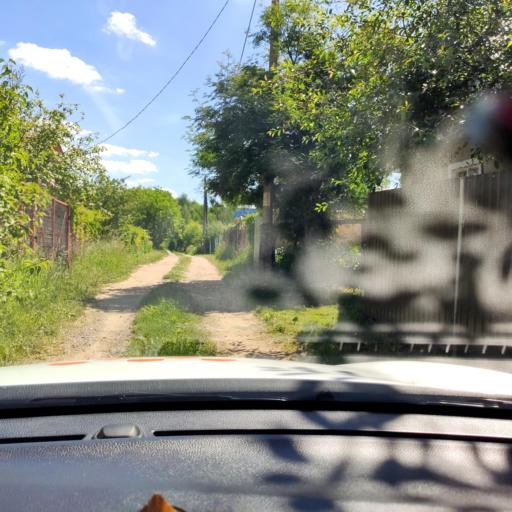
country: RU
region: Tatarstan
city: Vysokaya Gora
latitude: 55.8125
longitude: 49.2859
